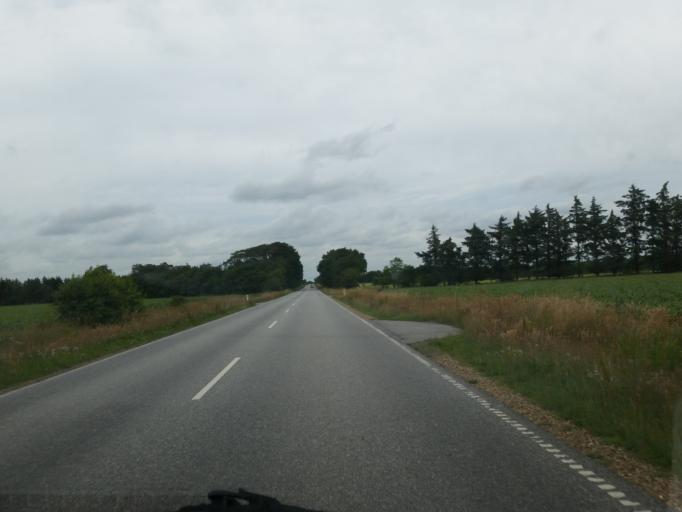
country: DK
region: South Denmark
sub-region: Esbjerg Kommune
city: Ribe
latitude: 55.3605
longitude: 8.7960
